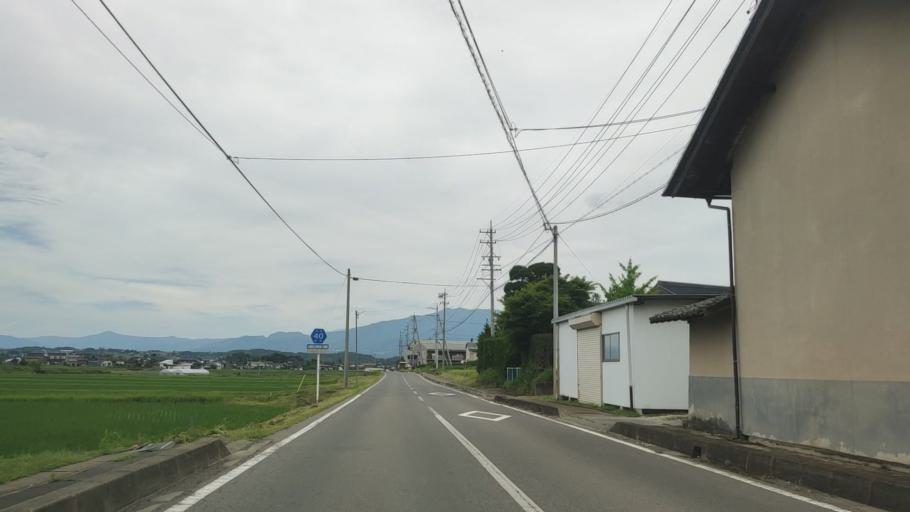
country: JP
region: Nagano
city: Kamimaruko
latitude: 36.2924
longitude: 138.3166
